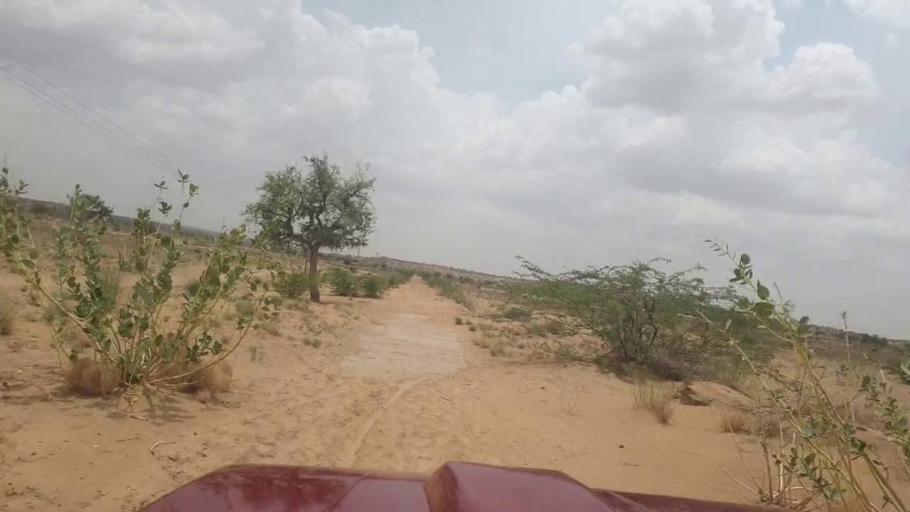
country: PK
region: Sindh
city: Islamkot
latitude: 25.1109
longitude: 70.3717
